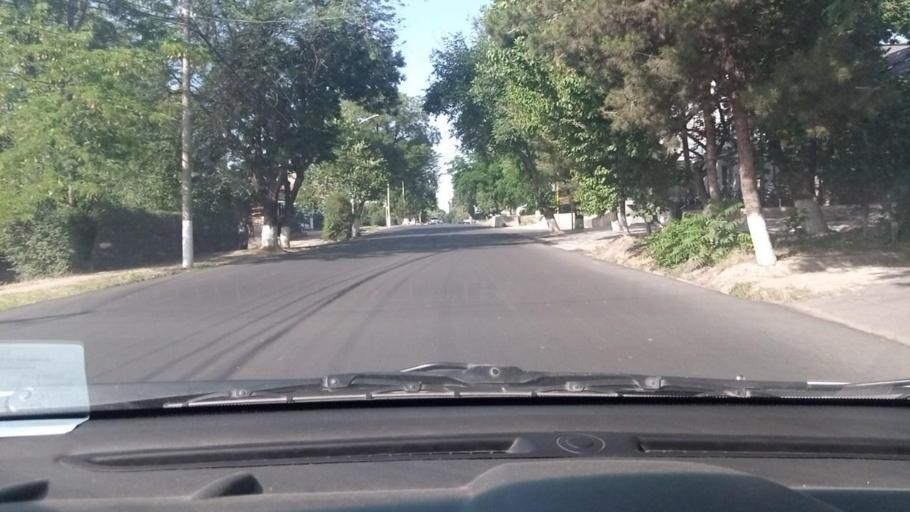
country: UZ
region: Toshkent
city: Salor
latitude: 41.3198
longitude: 69.3419
